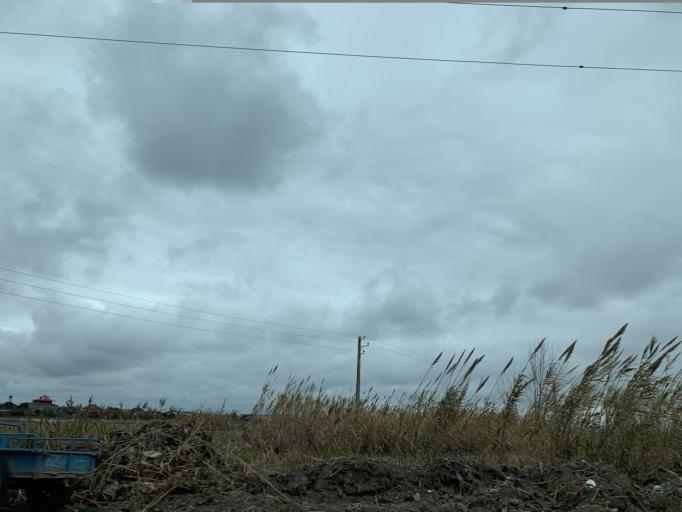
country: IR
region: Mazandaran
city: Babol
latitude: 36.5056
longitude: 52.5373
